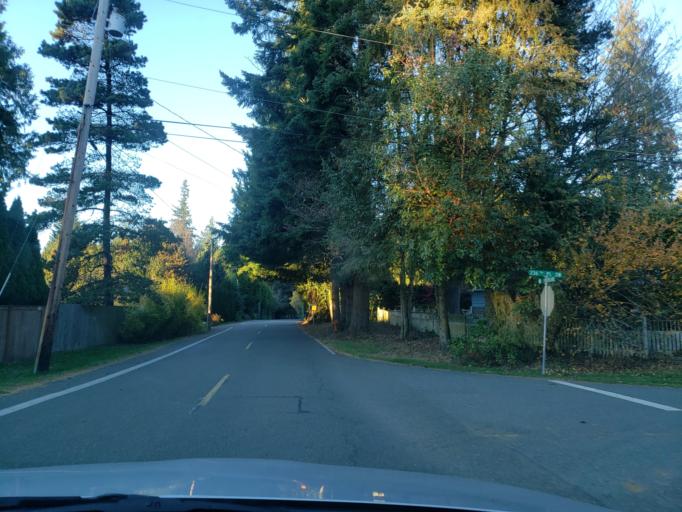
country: US
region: Washington
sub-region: Snohomish County
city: Woodway
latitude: 47.7846
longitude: -122.3829
